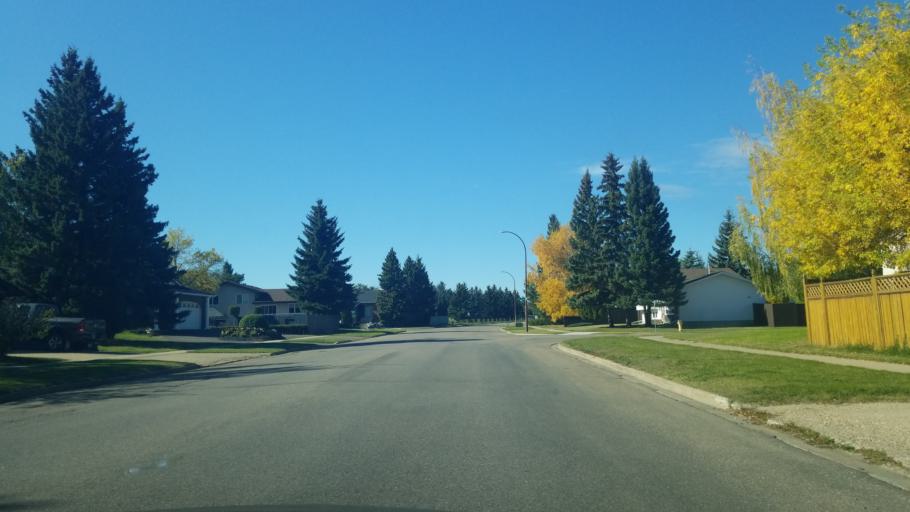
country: CA
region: Saskatchewan
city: Lloydminster
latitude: 53.2731
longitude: -110.0131
